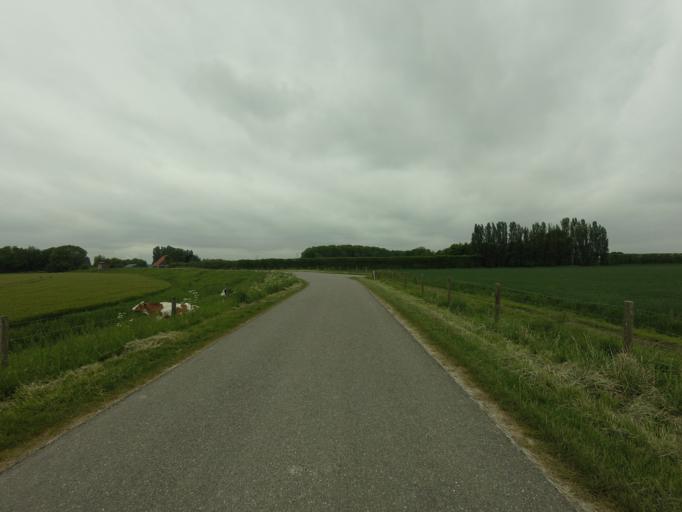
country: NL
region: South Holland
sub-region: Gemeente Spijkenisse
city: Spijkenisse
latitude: 51.7962
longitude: 4.3430
